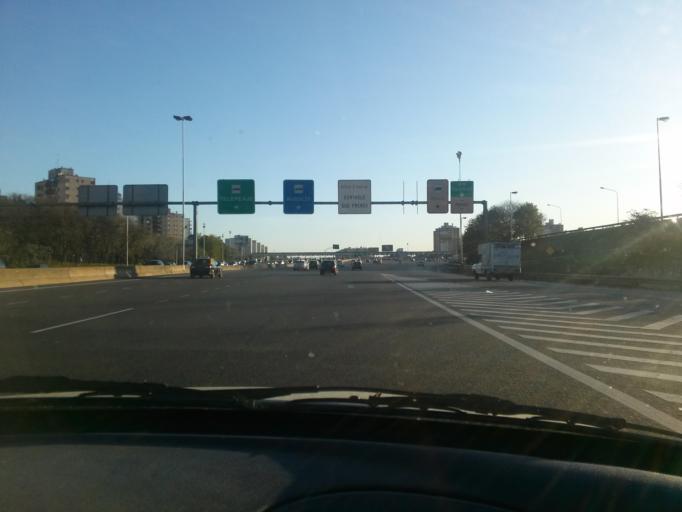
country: AR
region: Buenos Aires F.D.
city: Villa Lugano
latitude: -34.6954
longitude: -58.4925
